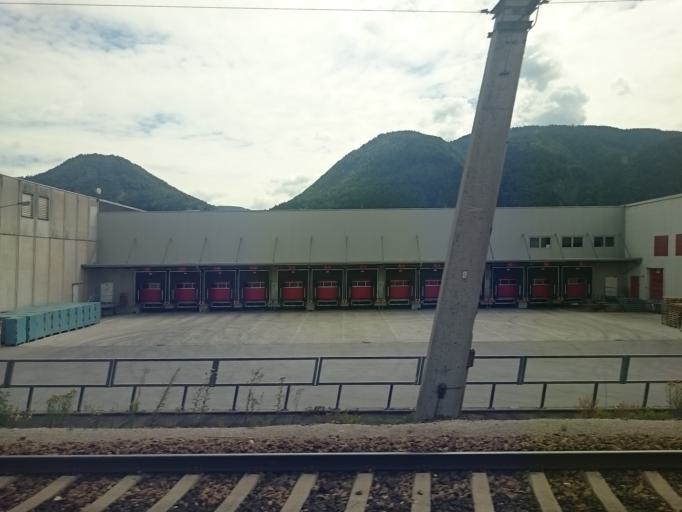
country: AT
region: Tyrol
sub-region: Politischer Bezirk Kufstein
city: Worgl
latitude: 47.4871
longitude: 12.0525
